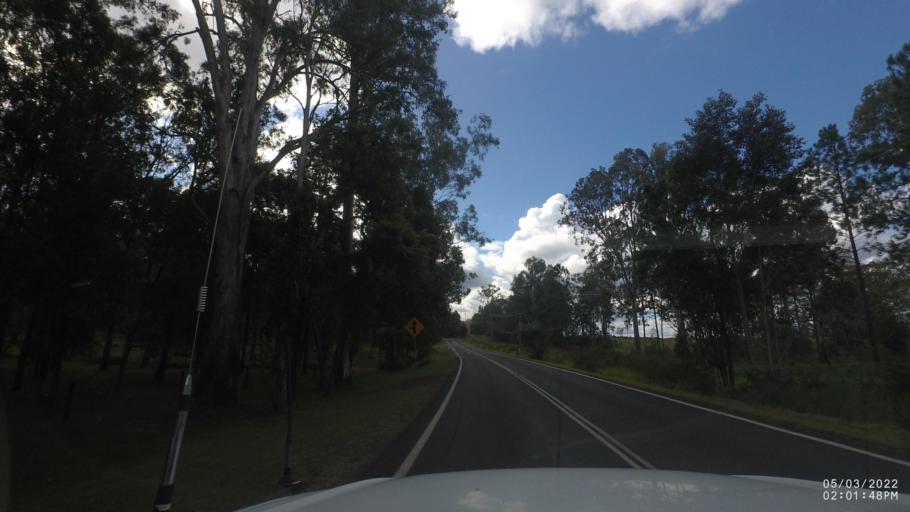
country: AU
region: Queensland
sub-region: Logan
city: Chambers Flat
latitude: -27.8107
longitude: 153.0975
